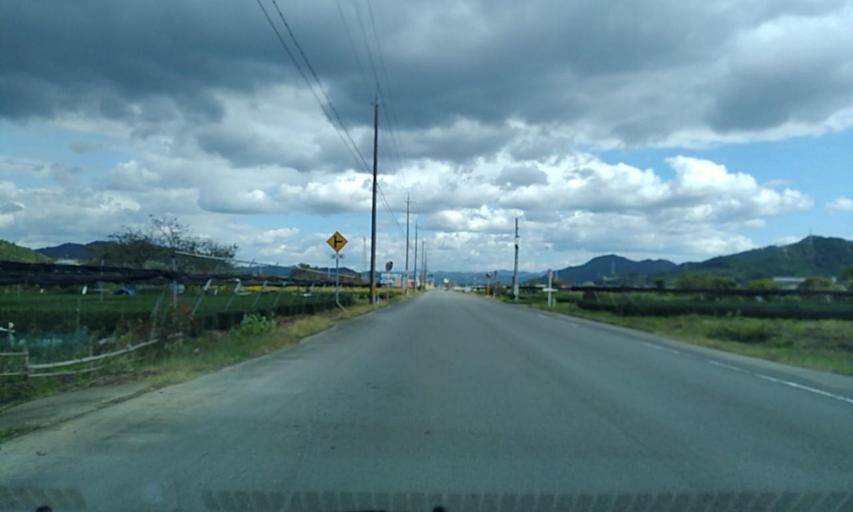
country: JP
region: Kyoto
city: Fukuchiyama
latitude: 35.3050
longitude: 135.1665
